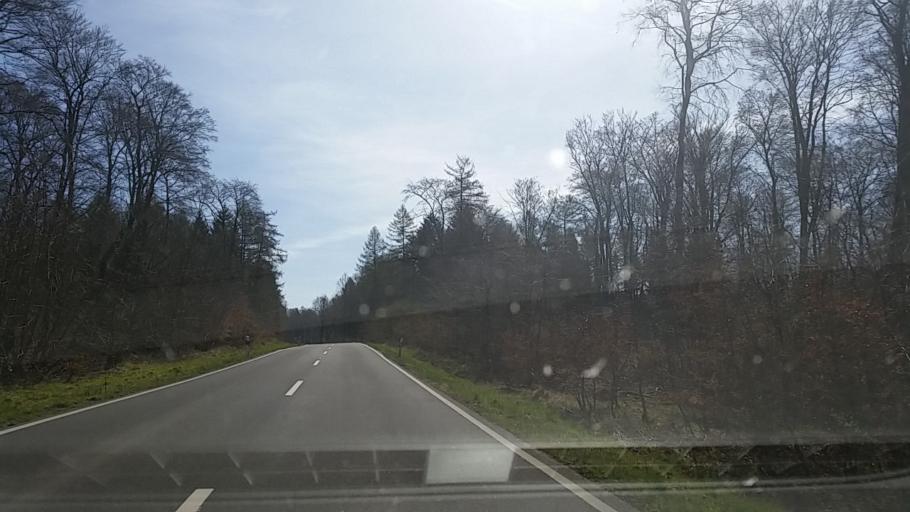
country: DE
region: Lower Saxony
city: Rabke
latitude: 52.1668
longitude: 10.8721
